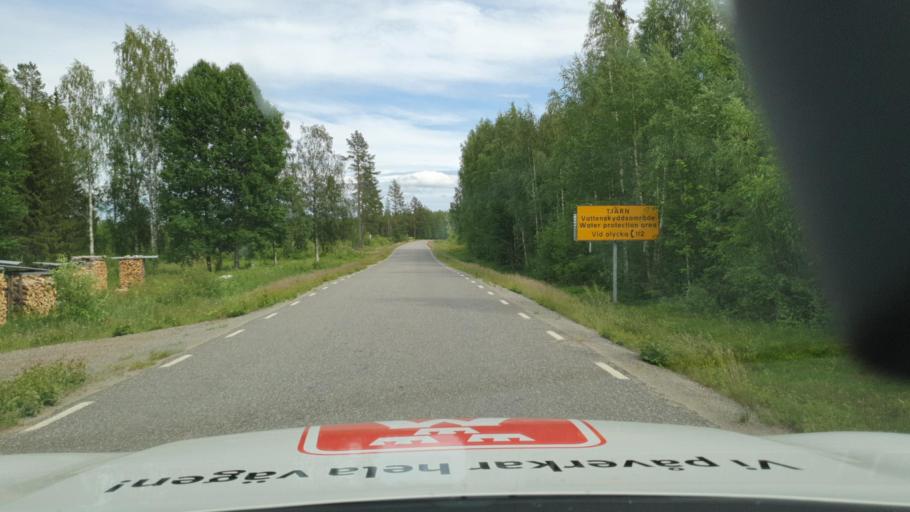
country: SE
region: Vaesterbotten
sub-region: Skelleftea Kommun
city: Viken
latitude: 64.4979
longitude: 20.8919
